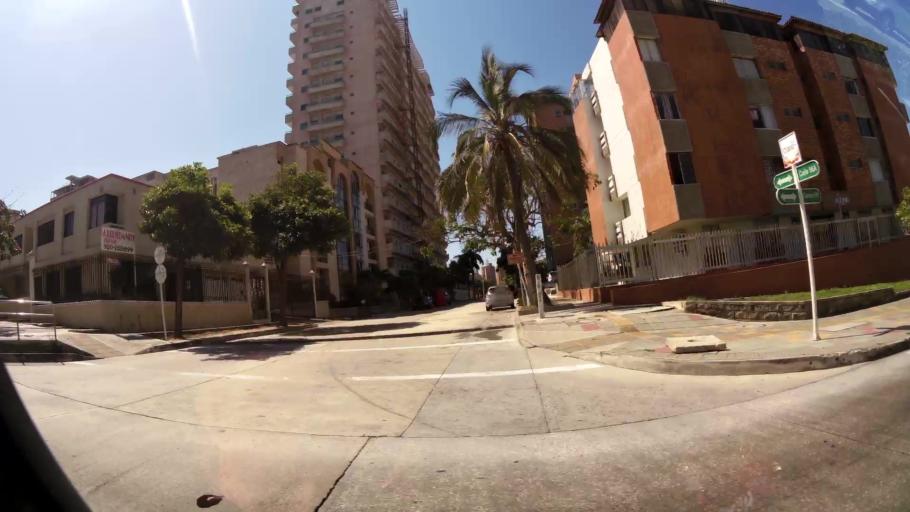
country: CO
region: Atlantico
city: Barranquilla
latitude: 11.0105
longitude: -74.8276
